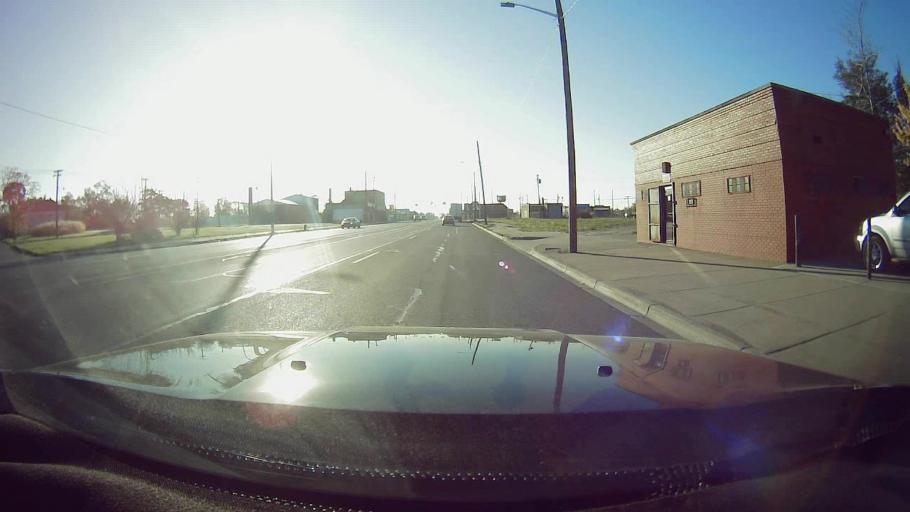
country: US
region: Michigan
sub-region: Wayne County
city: Hamtramck
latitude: 42.3890
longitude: -83.0223
